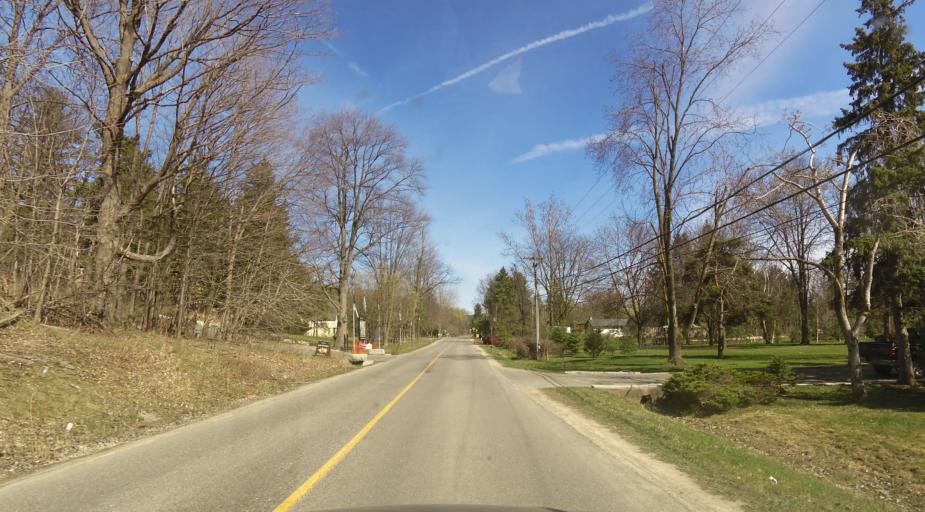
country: CA
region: Ontario
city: Brampton
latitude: 43.6473
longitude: -79.7778
